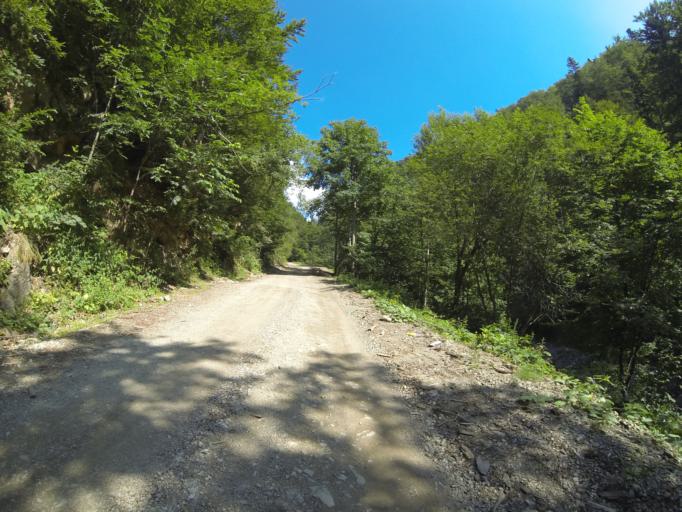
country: RO
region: Valcea
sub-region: Comuna Costesti
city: Bistrita
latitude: 45.2460
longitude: 23.9950
